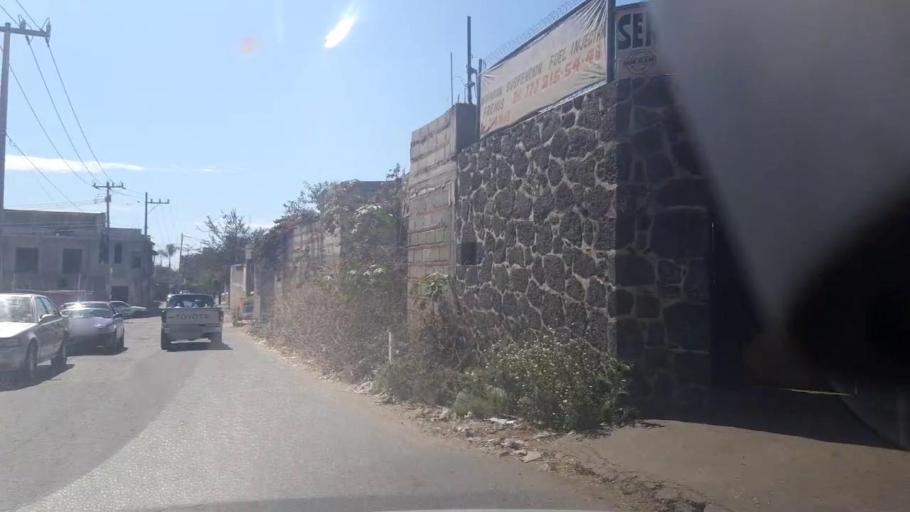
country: MX
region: Morelos
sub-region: Cuernavaca
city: Colonia los Cerritos
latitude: 18.9593
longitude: -99.2127
